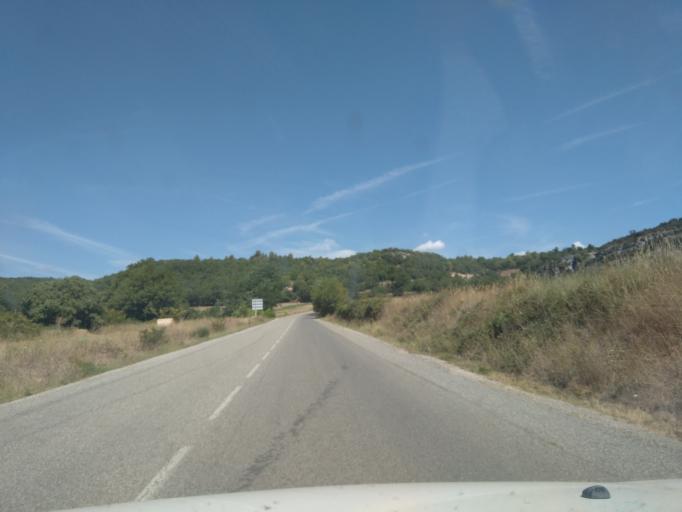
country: FR
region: Provence-Alpes-Cote d'Azur
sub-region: Departement du Var
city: Regusse
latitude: 43.7053
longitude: 6.0420
